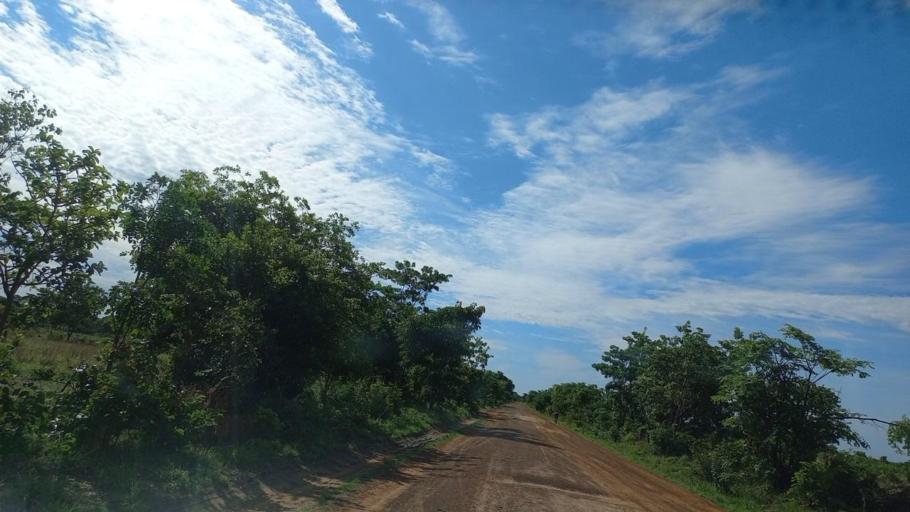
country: ZM
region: North-Western
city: Kabompo
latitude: -13.4347
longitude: 24.4204
